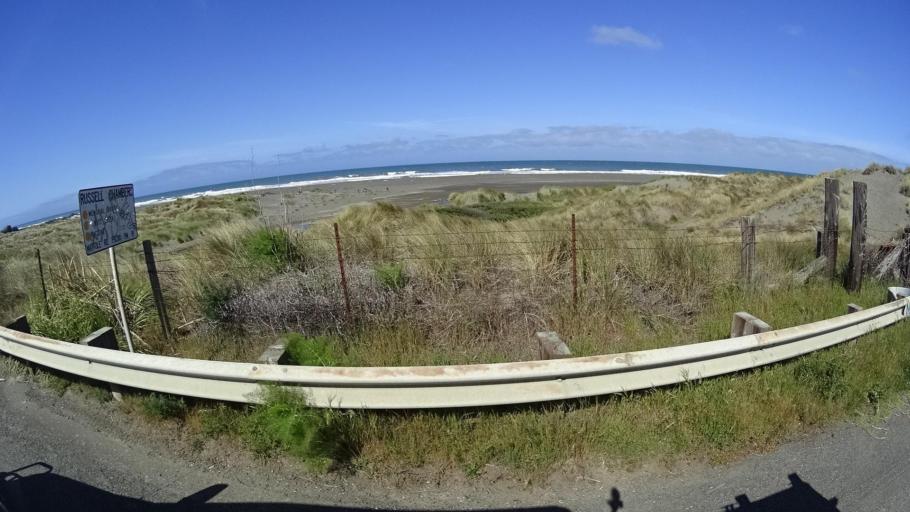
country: US
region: California
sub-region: Humboldt County
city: Ferndale
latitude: 40.3540
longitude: -124.3614
